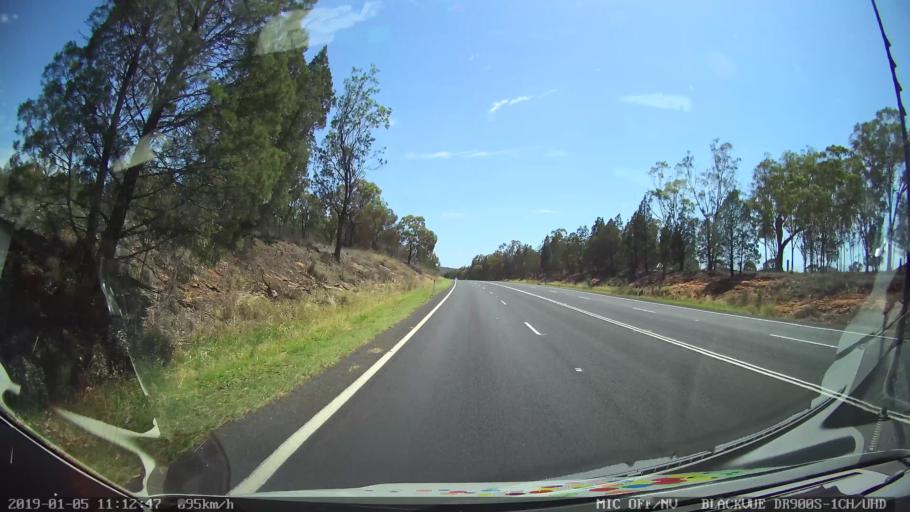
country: AU
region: New South Wales
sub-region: Warrumbungle Shire
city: Coonabarabran
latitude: -31.3784
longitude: 149.2645
